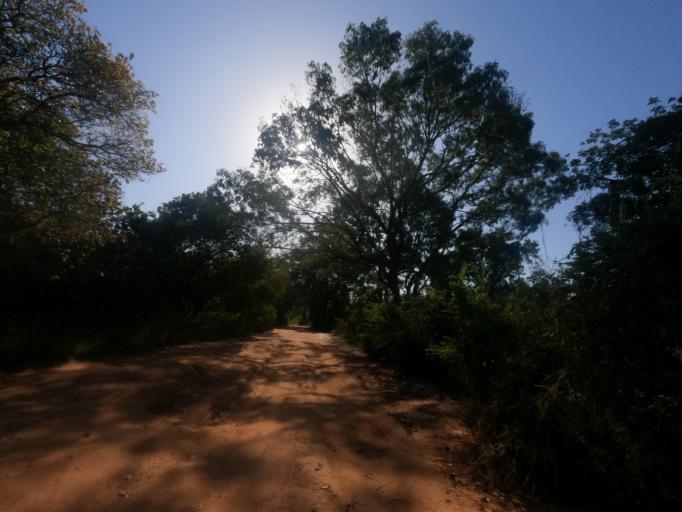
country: GW
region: Cacheu
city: Cacheu
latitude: 12.3989
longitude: -16.2110
